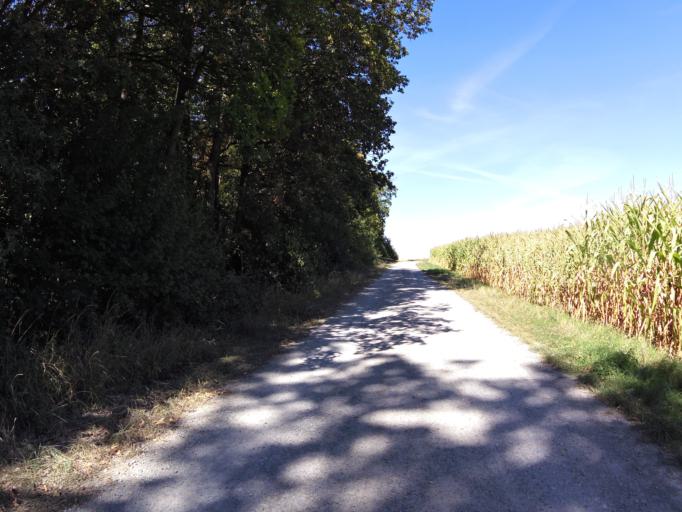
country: DE
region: Bavaria
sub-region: Regierungsbezirk Unterfranken
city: Guntersleben
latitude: 49.8619
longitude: 9.8865
